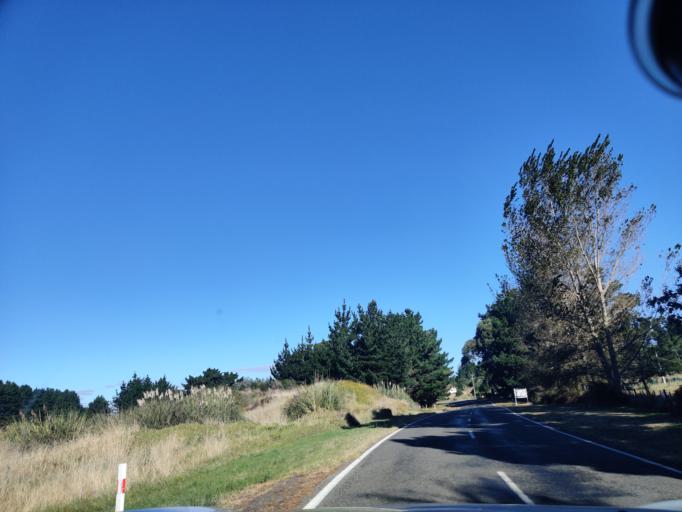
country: NZ
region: Manawatu-Wanganui
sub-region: Horowhenua District
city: Foxton
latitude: -40.3724
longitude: 175.2472
